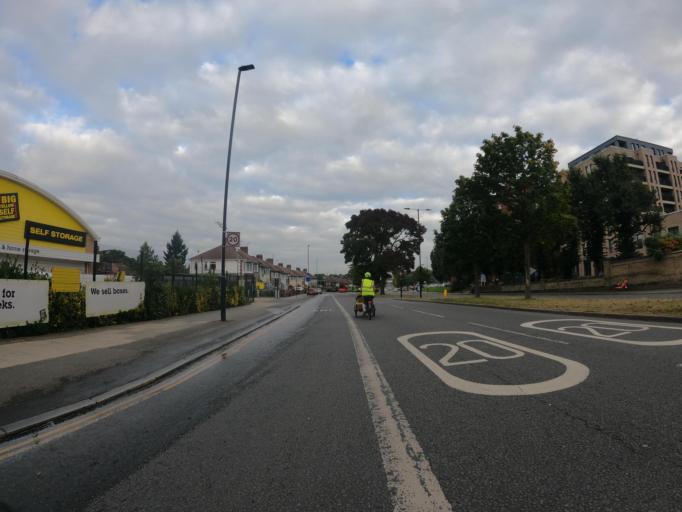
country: GB
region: England
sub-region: Greater London
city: Greenford
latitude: 51.5091
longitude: -0.3493
